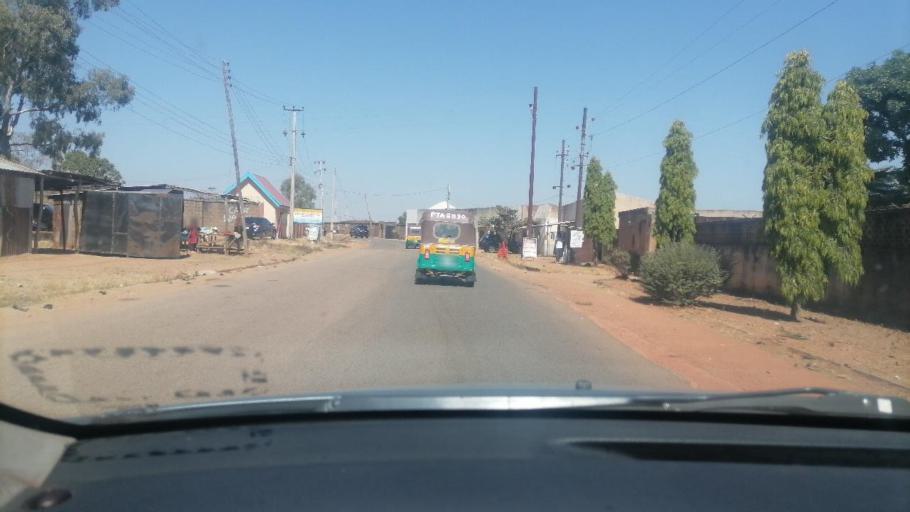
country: NG
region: Plateau
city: Jos
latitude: 9.8708
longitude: 8.9064
